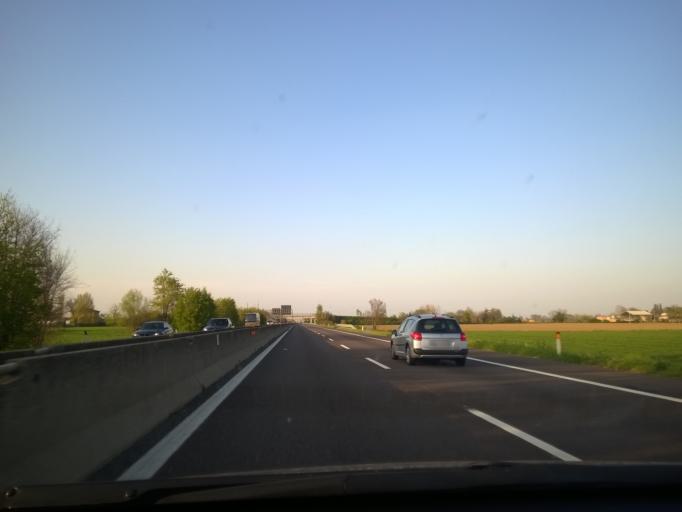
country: IT
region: Emilia-Romagna
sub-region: Provincia di Bologna
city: Progresso
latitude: 44.5448
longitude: 11.3695
